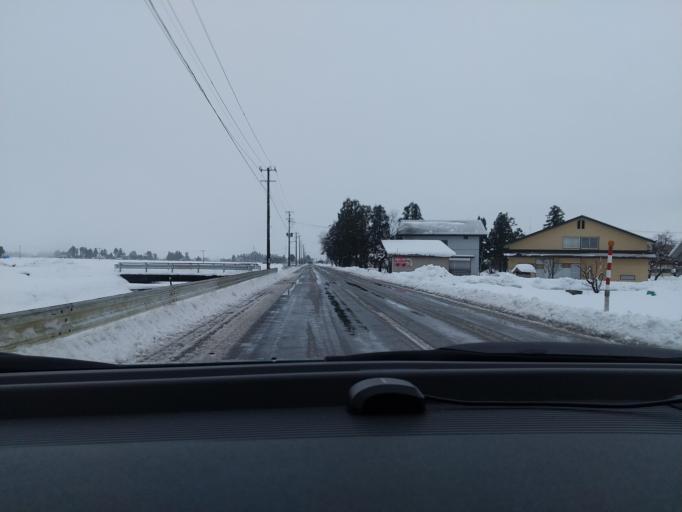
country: JP
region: Akita
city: Kakunodatemachi
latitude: 39.5244
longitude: 140.5580
